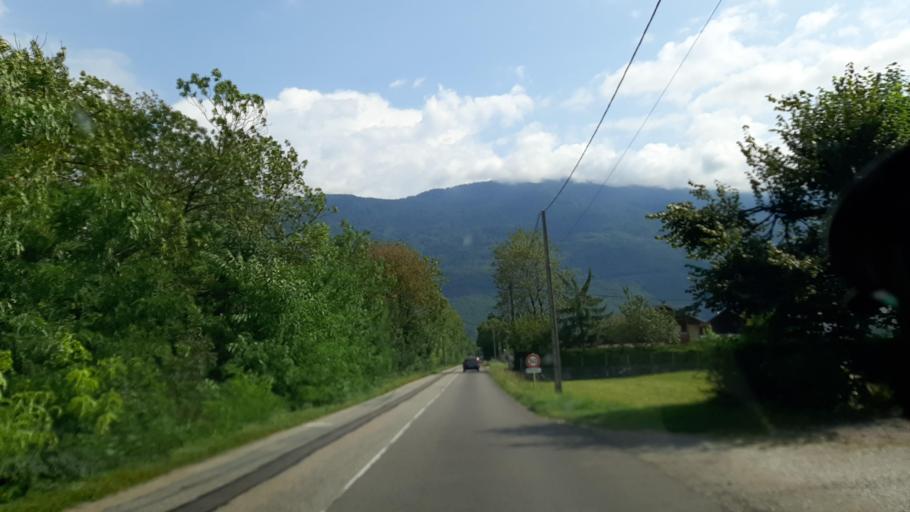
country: FR
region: Rhone-Alpes
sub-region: Departement de la Savoie
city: Gilly-sur-Isere
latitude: 45.6667
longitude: 6.3555
